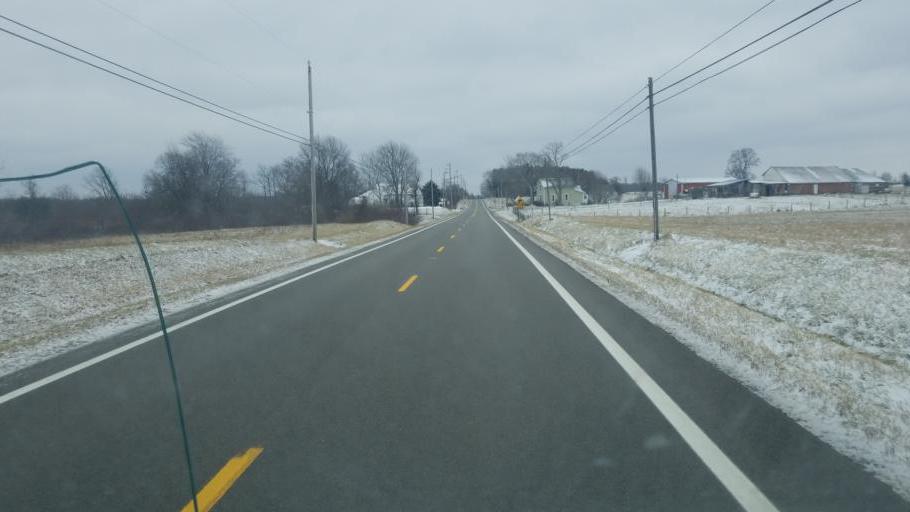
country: US
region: Ohio
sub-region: Licking County
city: Johnstown
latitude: 40.1734
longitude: -82.7217
